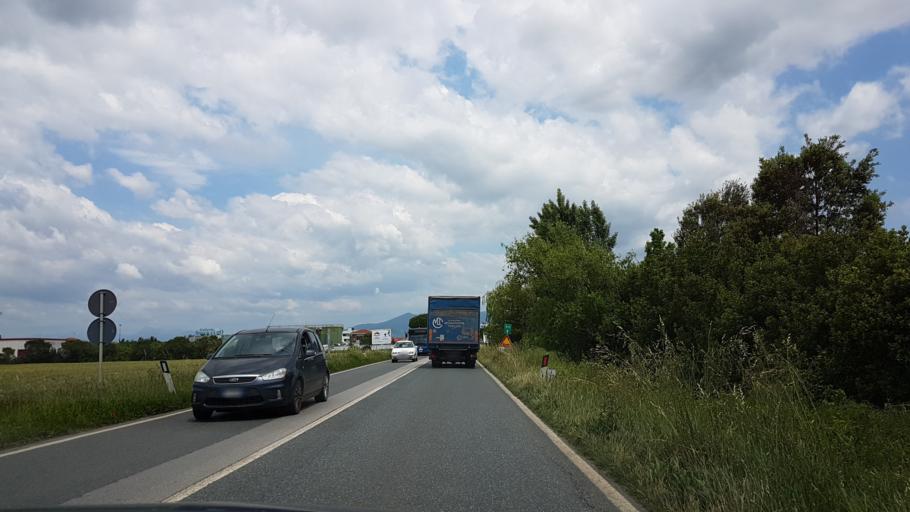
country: IT
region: Tuscany
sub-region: Provincia di Livorno
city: Collesalvetti
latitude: 43.5905
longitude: 10.4713
